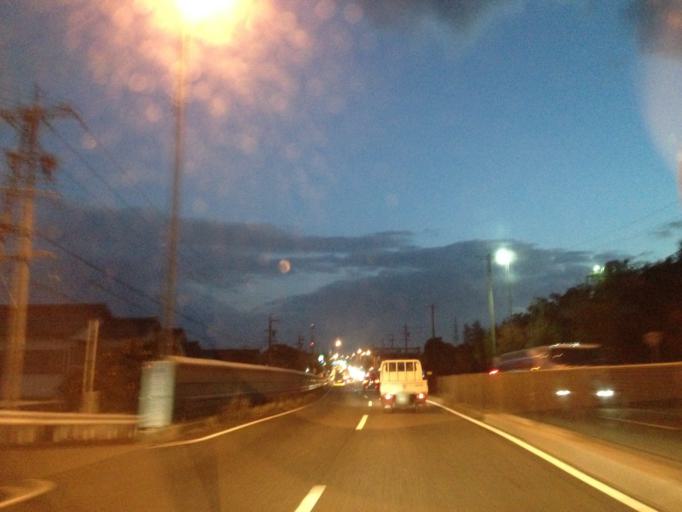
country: JP
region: Mie
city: Yokkaichi
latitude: 34.9685
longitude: 136.6380
